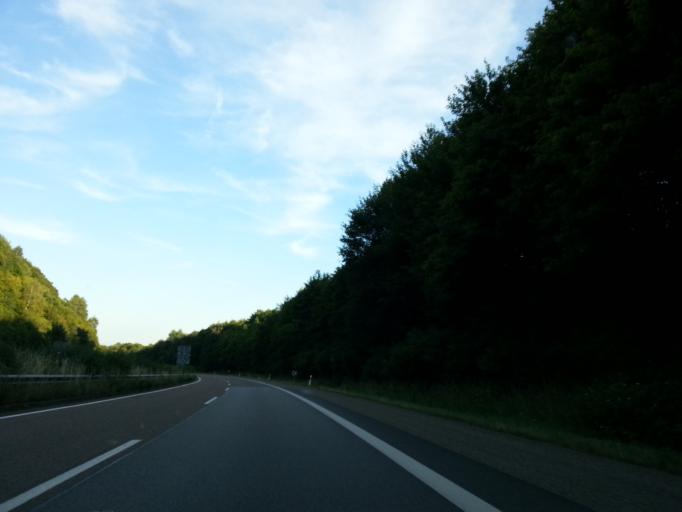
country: DE
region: Saarland
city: Freisen
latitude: 49.5444
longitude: 7.2583
